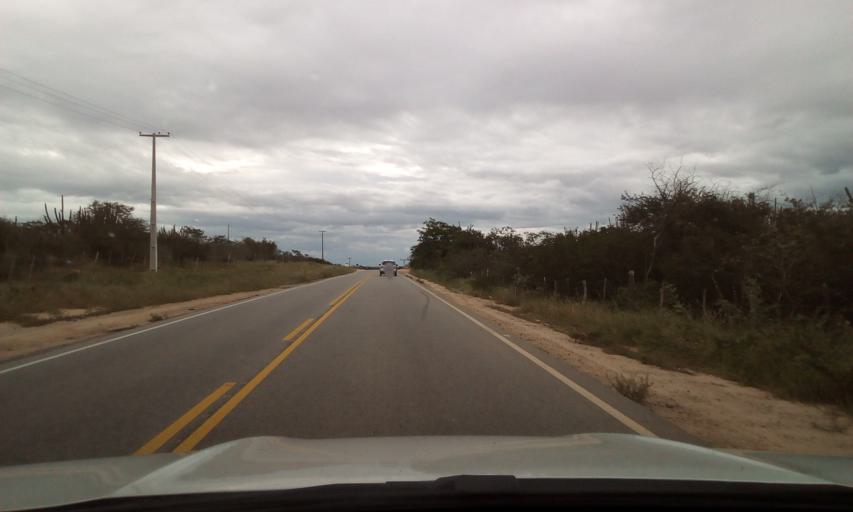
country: BR
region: Paraiba
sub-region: Picui
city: Picui
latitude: -6.5625
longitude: -36.2825
